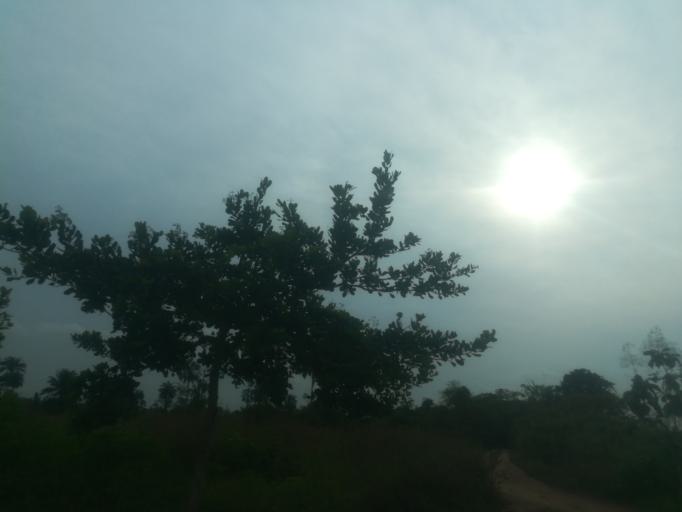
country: NG
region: Ogun
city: Ayetoro
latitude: 7.2511
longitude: 3.1177
